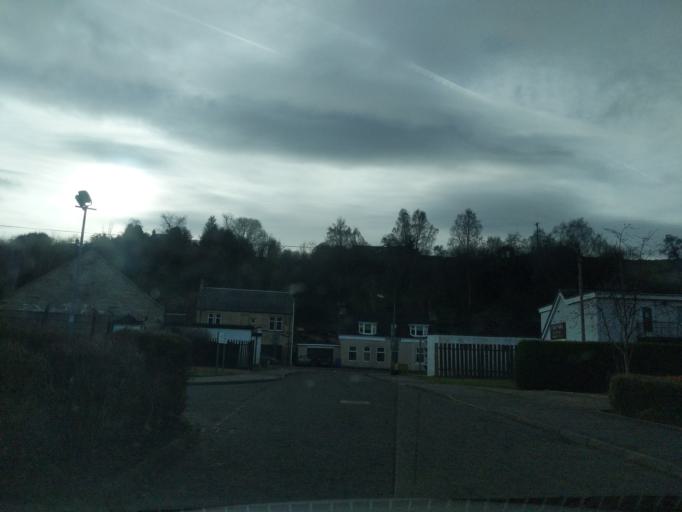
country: GB
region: Scotland
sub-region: South Lanarkshire
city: Law
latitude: 55.7002
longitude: -3.8700
